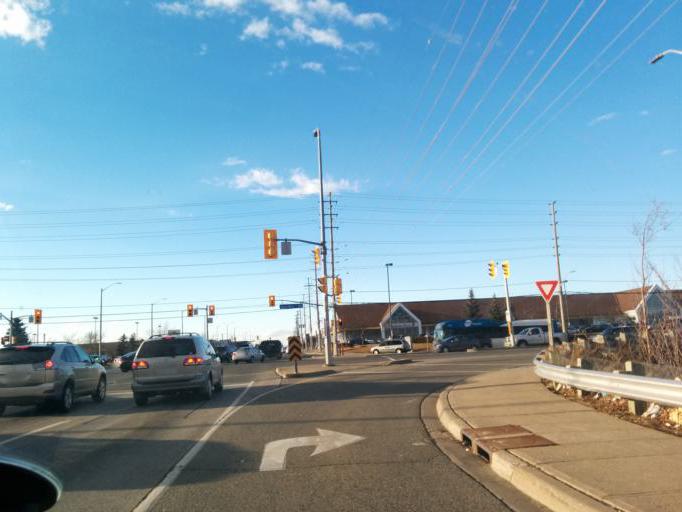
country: CA
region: Ontario
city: Mississauga
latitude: 43.5659
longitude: -79.6325
